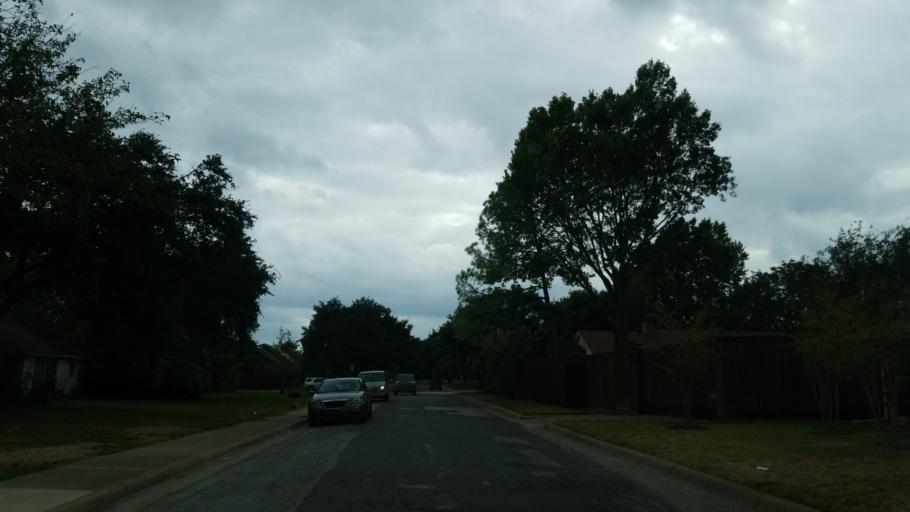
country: US
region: Texas
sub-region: Dallas County
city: Richardson
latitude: 32.9468
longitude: -96.7721
